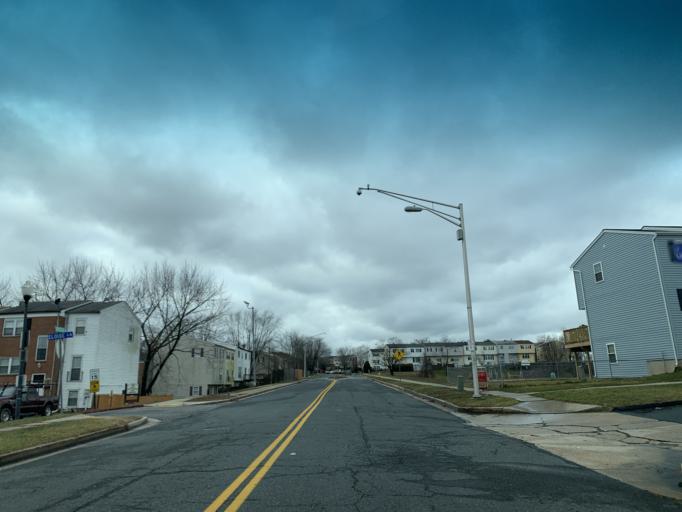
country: US
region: Maryland
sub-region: Harford County
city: Edgewood
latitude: 39.4330
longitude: -76.3142
